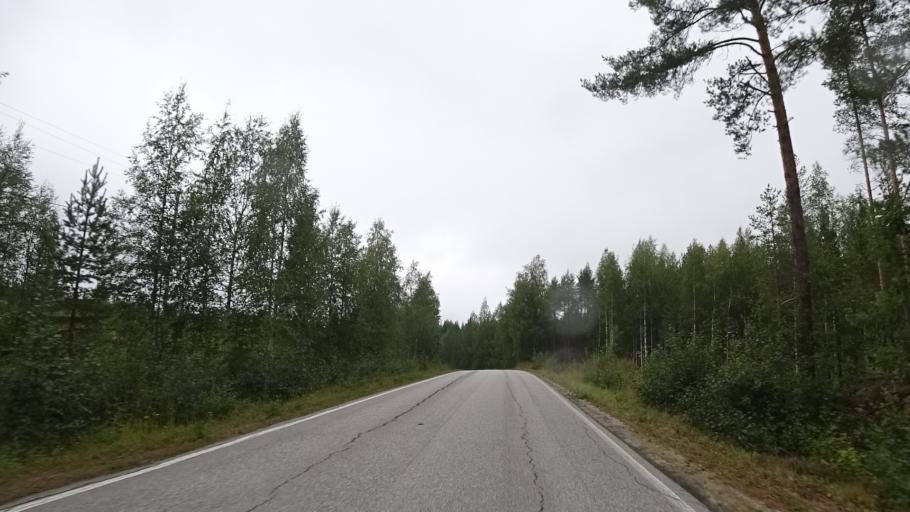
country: FI
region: North Karelia
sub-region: Pielisen Karjala
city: Lieksa
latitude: 63.3230
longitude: 30.2227
